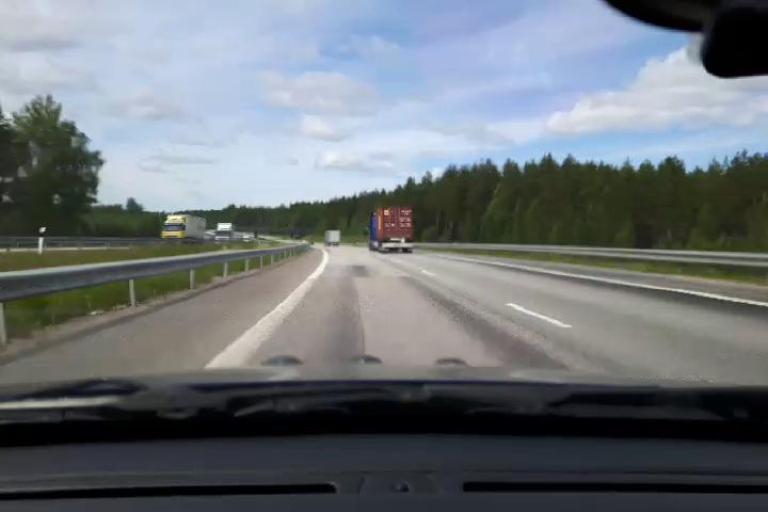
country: SE
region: Uppsala
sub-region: Alvkarleby Kommun
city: AElvkarleby
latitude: 60.4646
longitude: 17.4114
